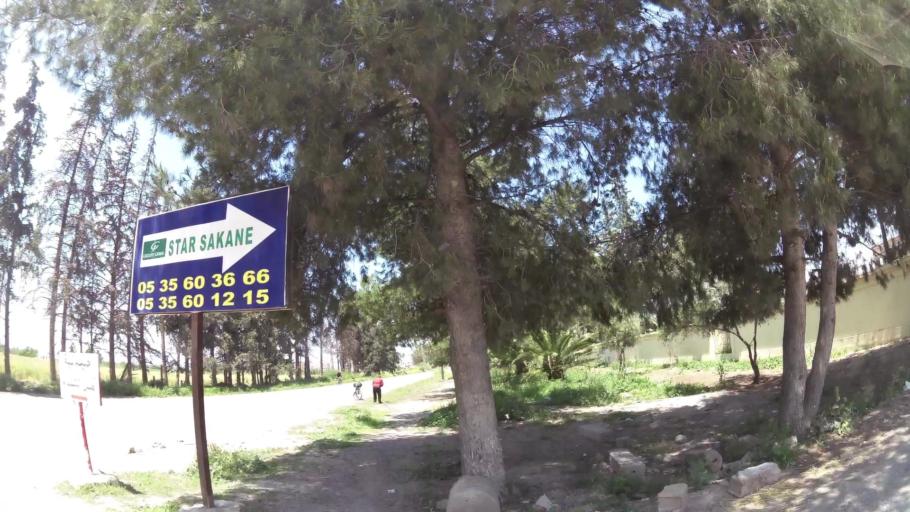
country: MA
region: Fes-Boulemane
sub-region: Fes
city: Fes
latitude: 34.0294
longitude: -5.0575
